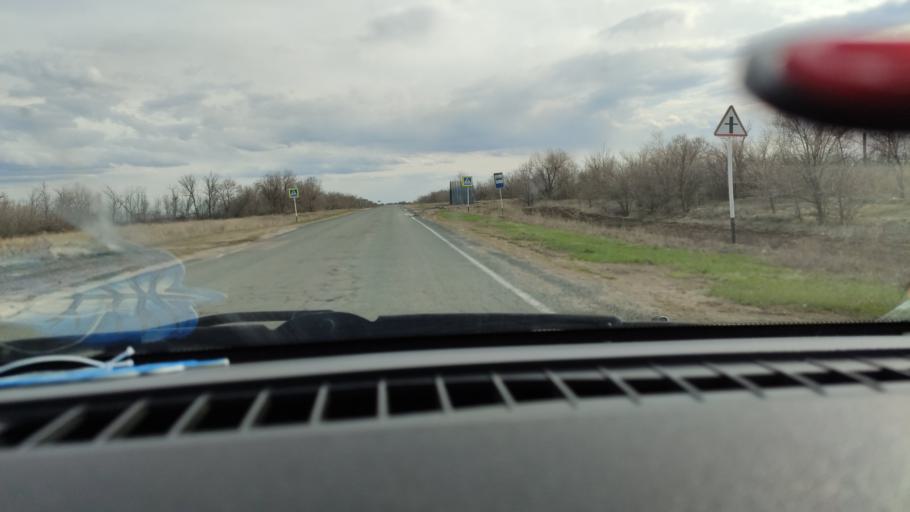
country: RU
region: Saratov
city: Rovnoye
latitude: 50.9678
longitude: 46.1169
